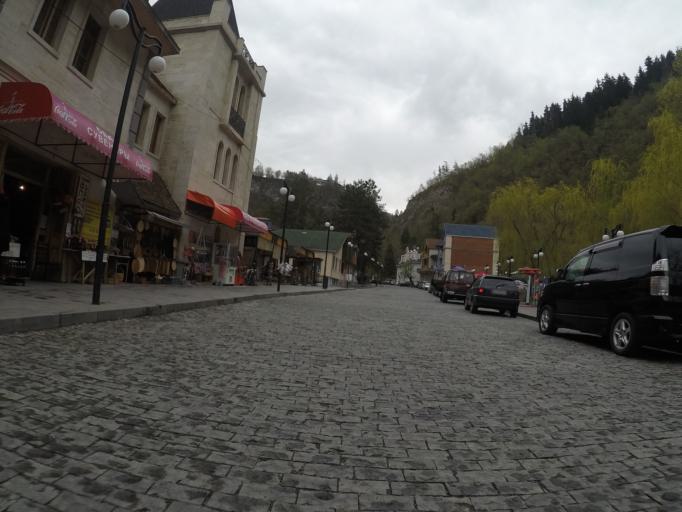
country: GE
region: Samtskhe-Javakheti
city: Borjomi
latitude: 41.8370
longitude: 43.3893
